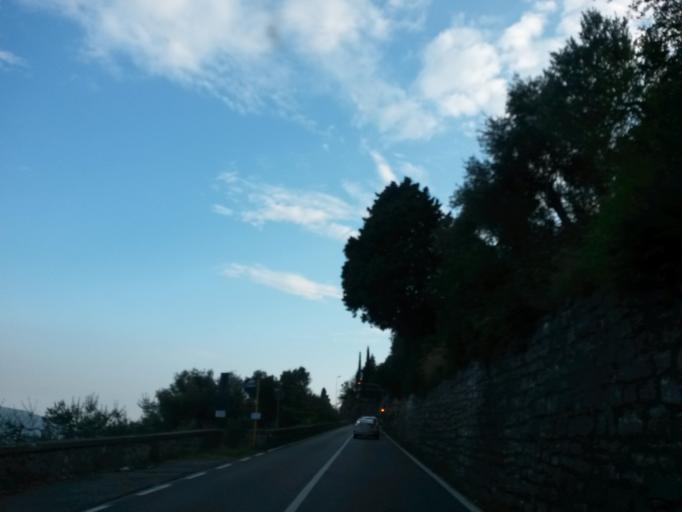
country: IT
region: Lombardy
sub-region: Provincia di Brescia
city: Gardola
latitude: 45.7137
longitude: 10.7010
